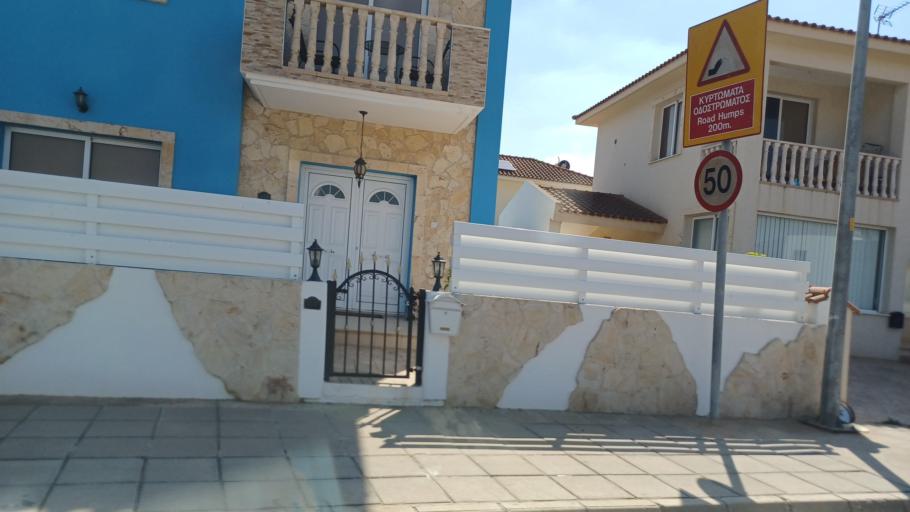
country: CY
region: Ammochostos
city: Acheritou
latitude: 35.0790
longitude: 33.8749
